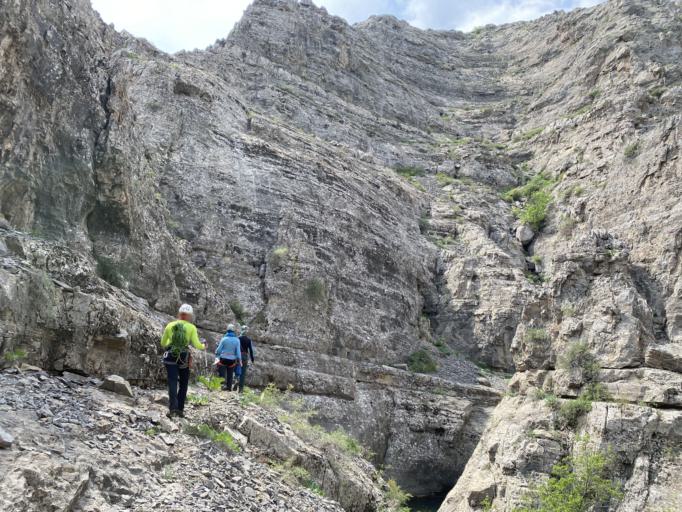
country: KZ
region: Ongtustik Qazaqstan
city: Ashchysay
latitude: 43.5331
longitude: 68.8442
